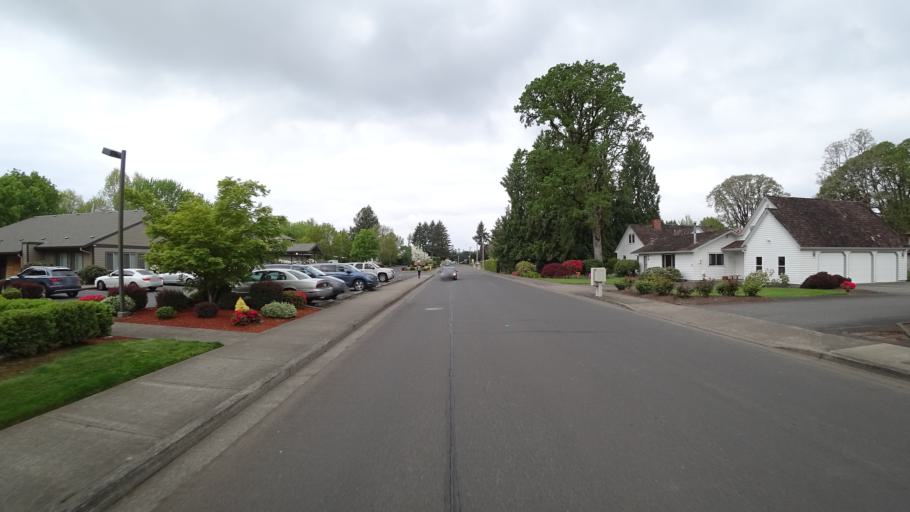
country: US
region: Oregon
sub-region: Washington County
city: Hillsboro
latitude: 45.5442
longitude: -122.9768
